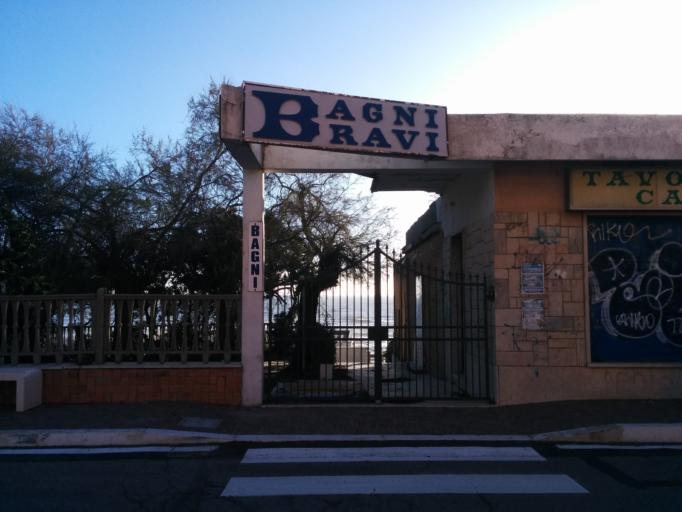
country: IT
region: Latium
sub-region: Citta metropolitana di Roma Capitale
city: Lavinio
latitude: 41.4967
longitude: 12.5858
